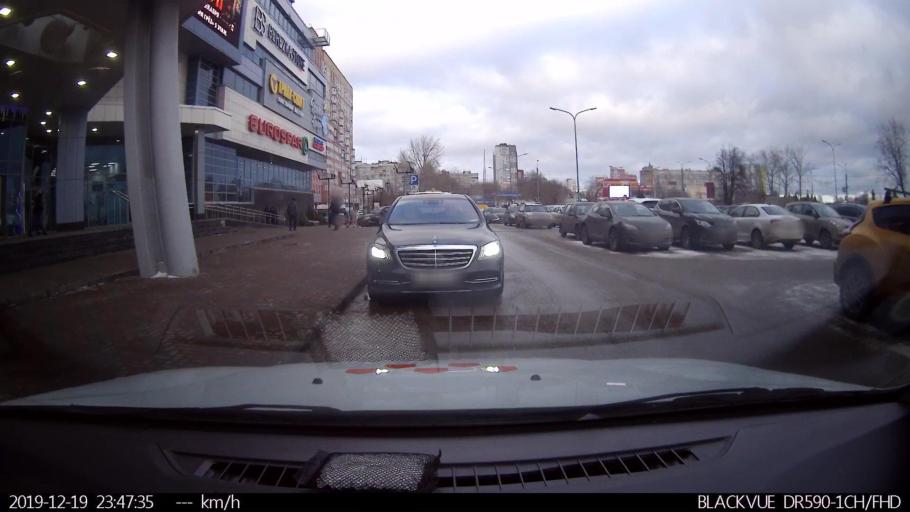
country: RU
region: Tverskaya
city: Ves'yegonsk
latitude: 58.7904
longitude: 37.0450
